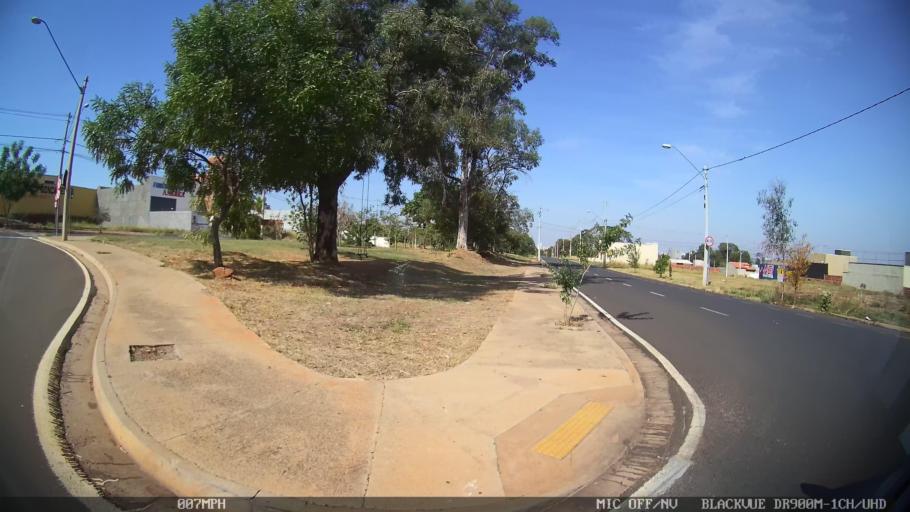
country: BR
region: Sao Paulo
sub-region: Sao Jose Do Rio Preto
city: Sao Jose do Rio Preto
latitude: -20.7837
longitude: -49.4273
